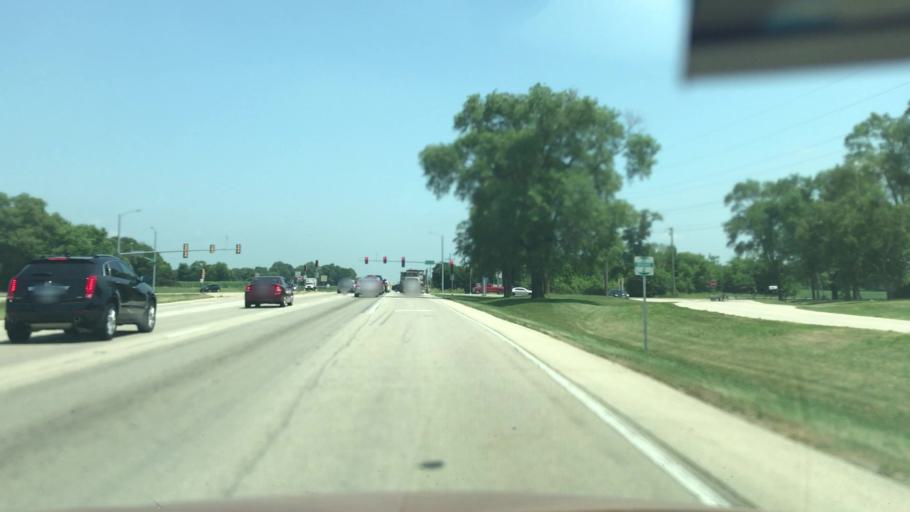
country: US
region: Illinois
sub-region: Winnebago County
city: Cherry Valley
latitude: 42.2398
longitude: -88.9024
